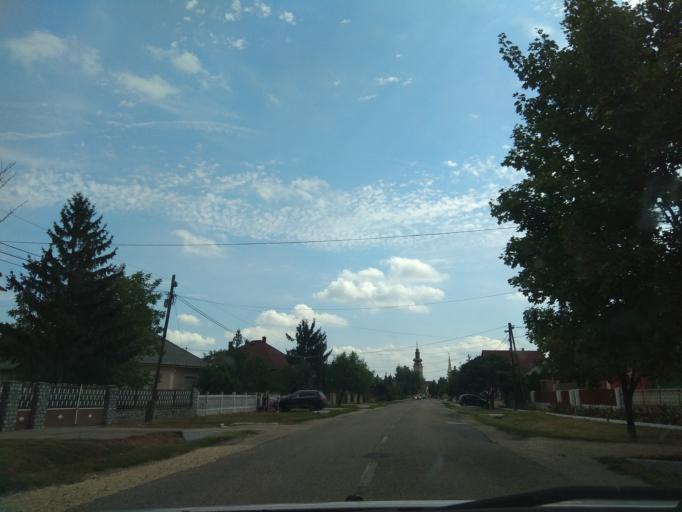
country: HU
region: Borsod-Abauj-Zemplen
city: Sajolad
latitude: 48.0386
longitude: 20.8864
